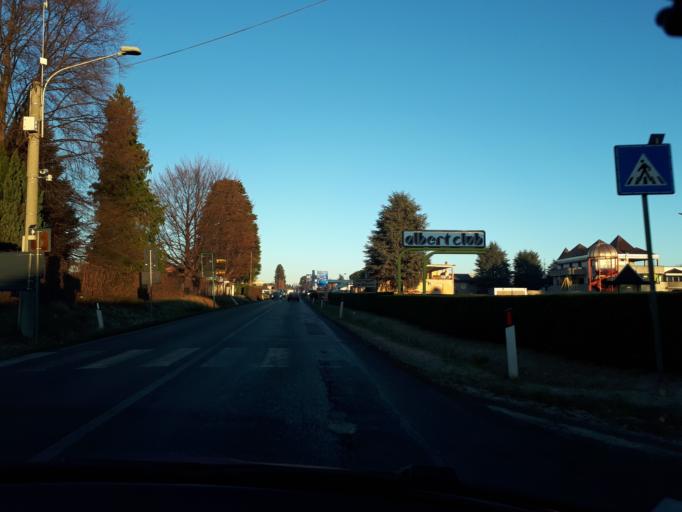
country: IT
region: Lombardy
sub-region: Provincia di Como
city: Vertemate Con Minoprio
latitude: 45.7290
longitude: 9.0644
